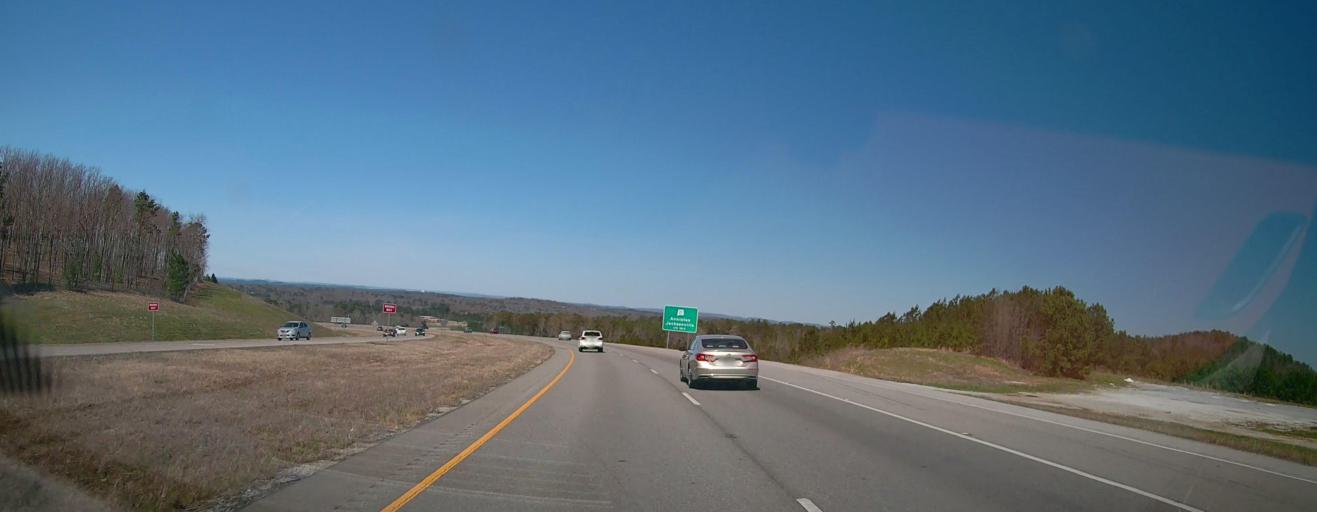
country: US
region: Alabama
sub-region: Calhoun County
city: Saks
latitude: 33.7002
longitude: -85.8089
